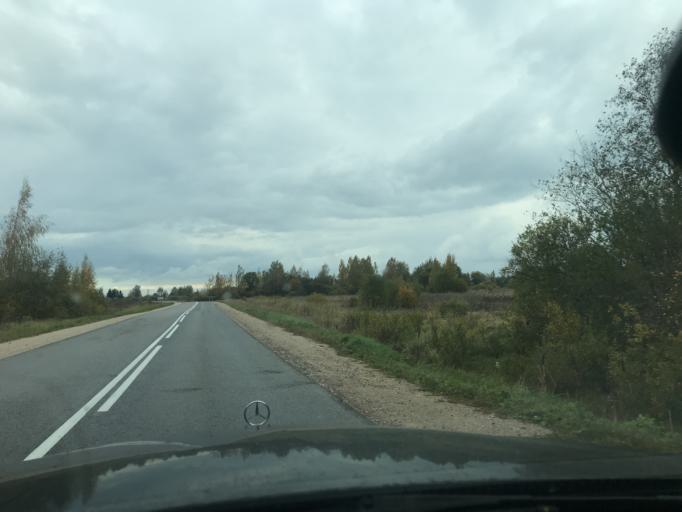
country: RU
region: Pskov
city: Izborsk
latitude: 57.6464
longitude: 27.9005
